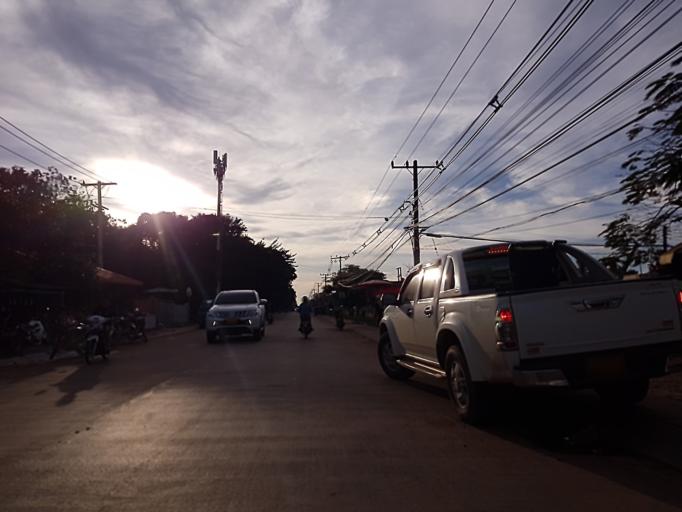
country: TH
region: Nong Khai
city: Si Chiang Mai
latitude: 18.0192
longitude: 102.5258
